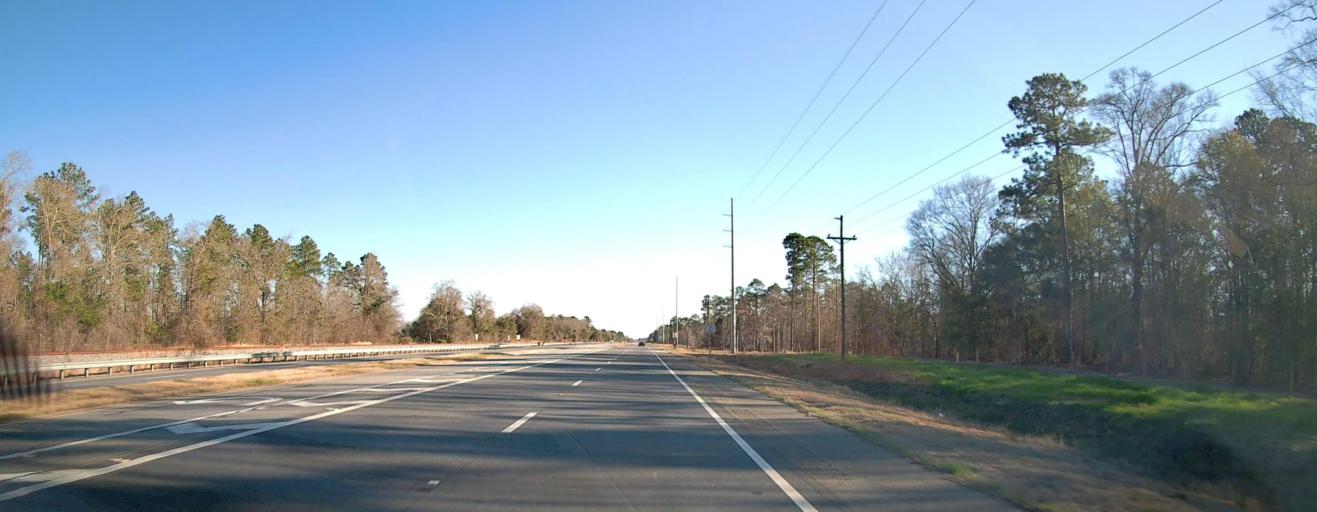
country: US
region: Georgia
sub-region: Lee County
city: Leesburg
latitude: 31.8501
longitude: -84.2282
